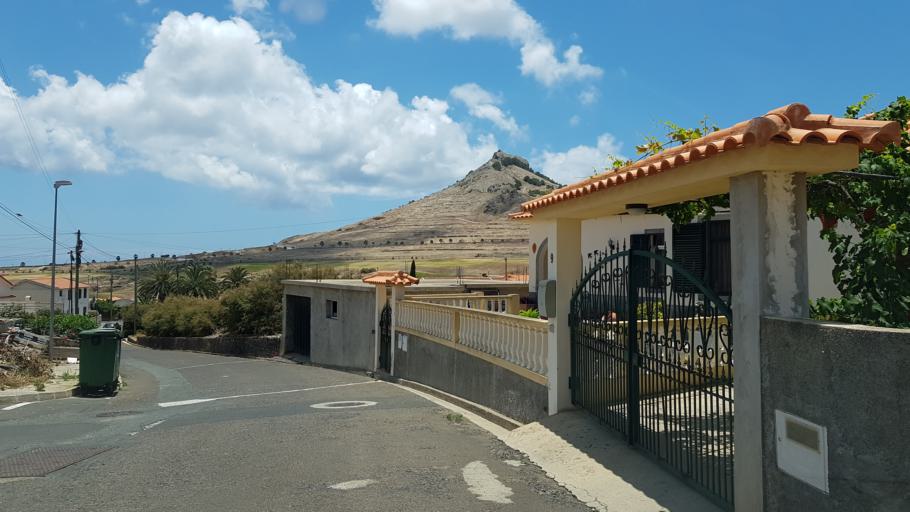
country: PT
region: Madeira
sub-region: Porto Santo
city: Vila de Porto Santo
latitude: 33.0556
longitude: -16.3658
